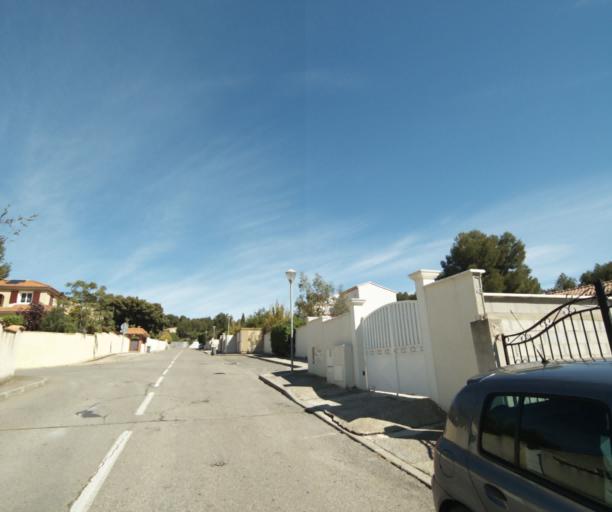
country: FR
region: Provence-Alpes-Cote d'Azur
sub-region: Departement des Bouches-du-Rhone
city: Rognac
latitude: 43.5104
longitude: 5.2108
